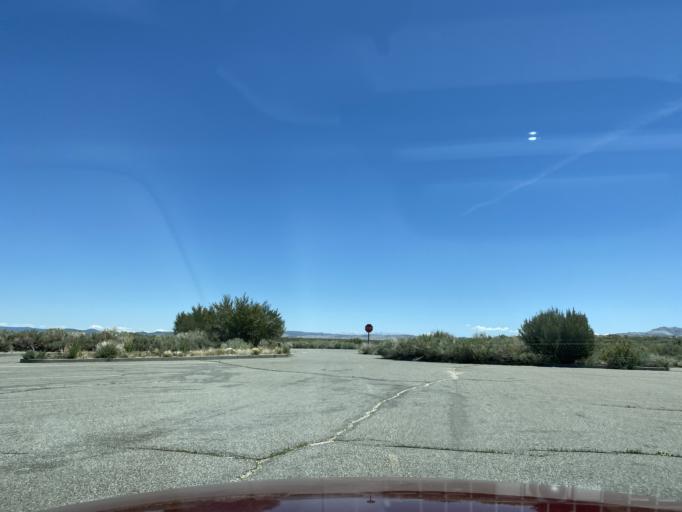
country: US
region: California
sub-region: Mono County
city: Bridgeport
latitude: 37.9659
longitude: -119.1209
